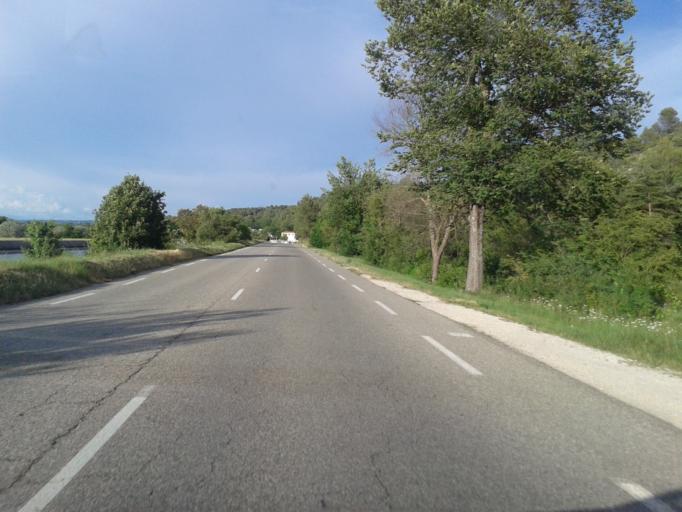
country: FR
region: Provence-Alpes-Cote d'Azur
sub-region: Departement du Vaucluse
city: Beaumont-de-Pertuis
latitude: 43.6870
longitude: 5.7156
